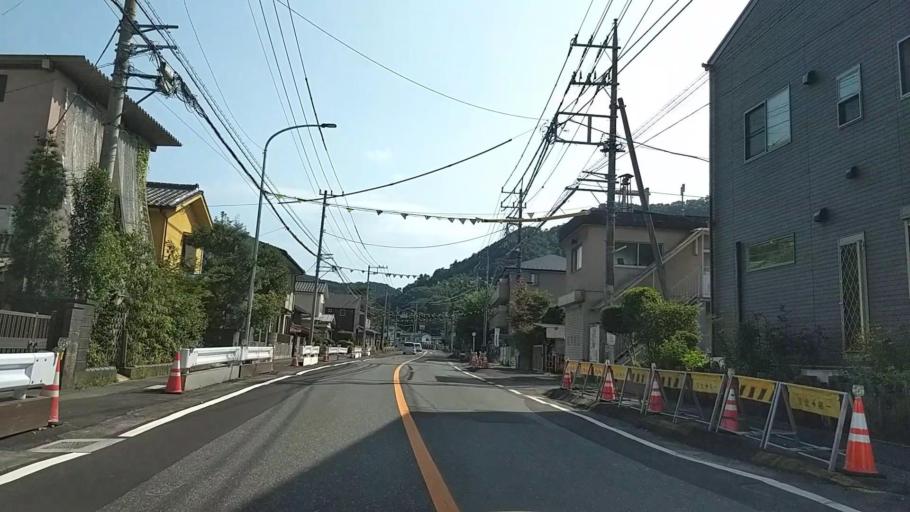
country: JP
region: Tokyo
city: Hachioji
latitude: 35.6377
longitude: 139.2711
